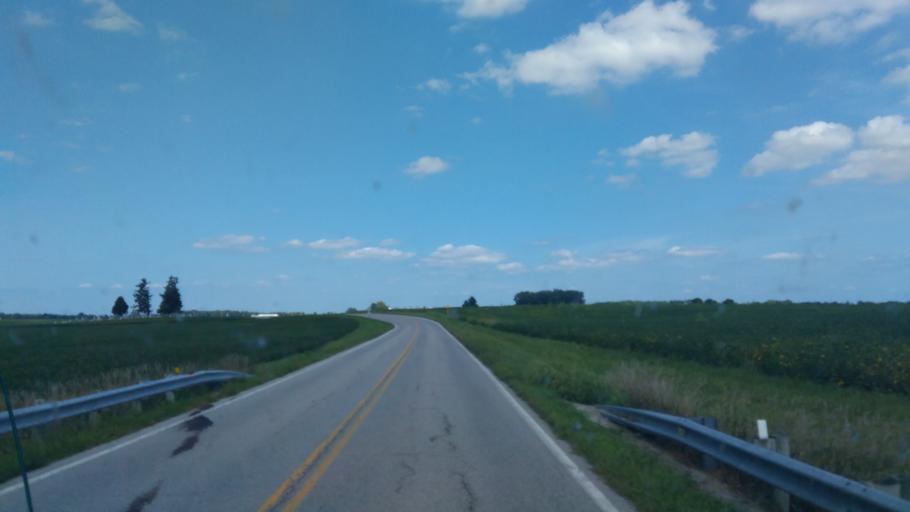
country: US
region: Ohio
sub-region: Union County
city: Richwood
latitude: 40.4358
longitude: -83.4023
